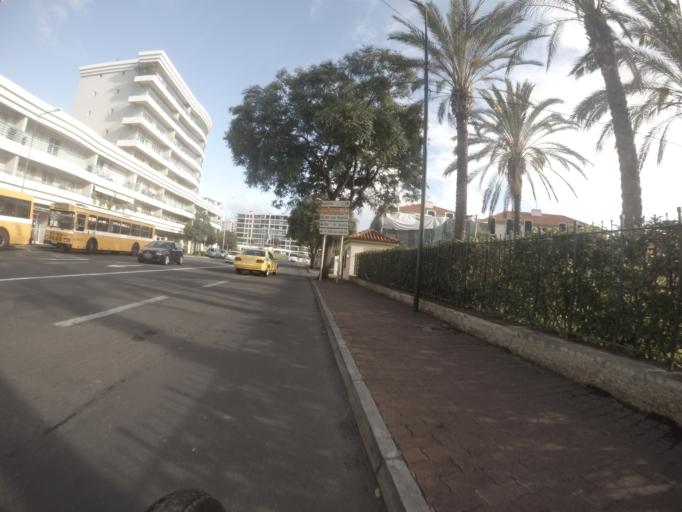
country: PT
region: Madeira
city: Camara de Lobos
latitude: 32.6414
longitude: -16.9497
